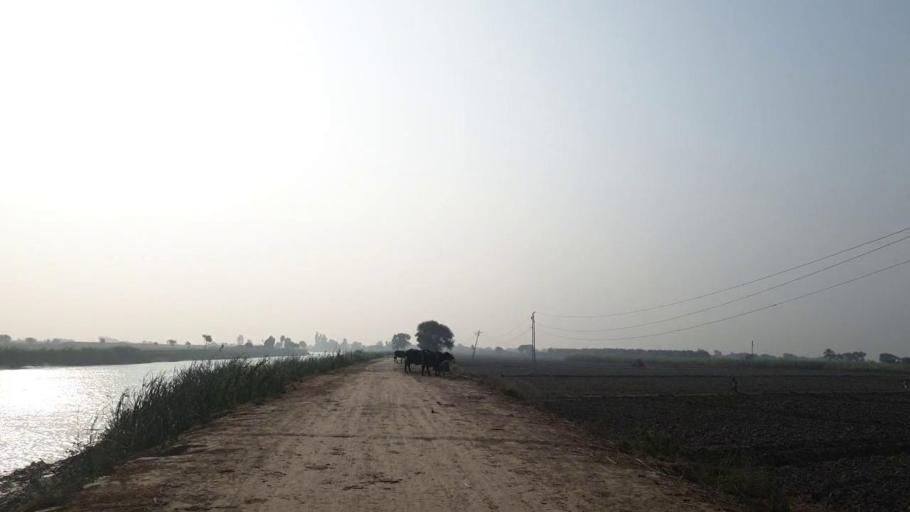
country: PK
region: Sindh
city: Tando Muhammad Khan
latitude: 25.0979
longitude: 68.5760
